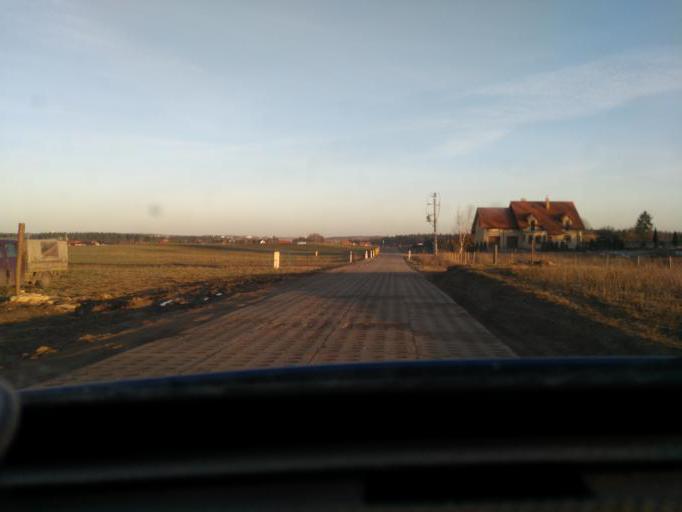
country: PL
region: Pomeranian Voivodeship
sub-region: Powiat kartuski
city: Banino
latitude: 54.3820
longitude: 18.3968
